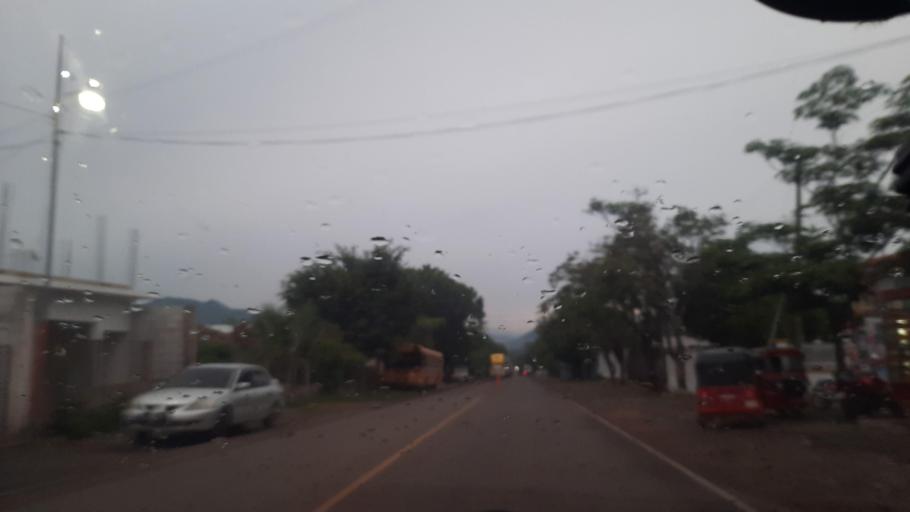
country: GT
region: Jutiapa
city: Atescatempa
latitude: 14.1902
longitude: -89.6701
